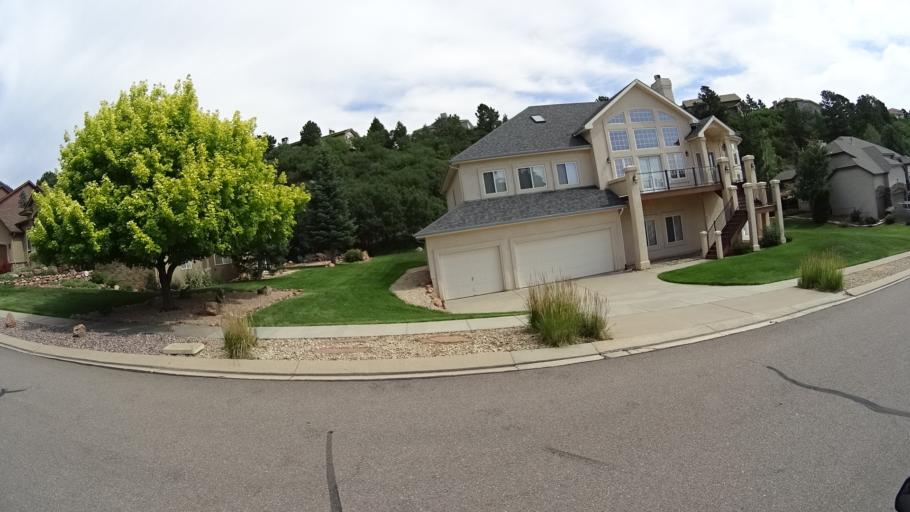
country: US
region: Colorado
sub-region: El Paso County
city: Air Force Academy
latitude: 38.9519
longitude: -104.8849
